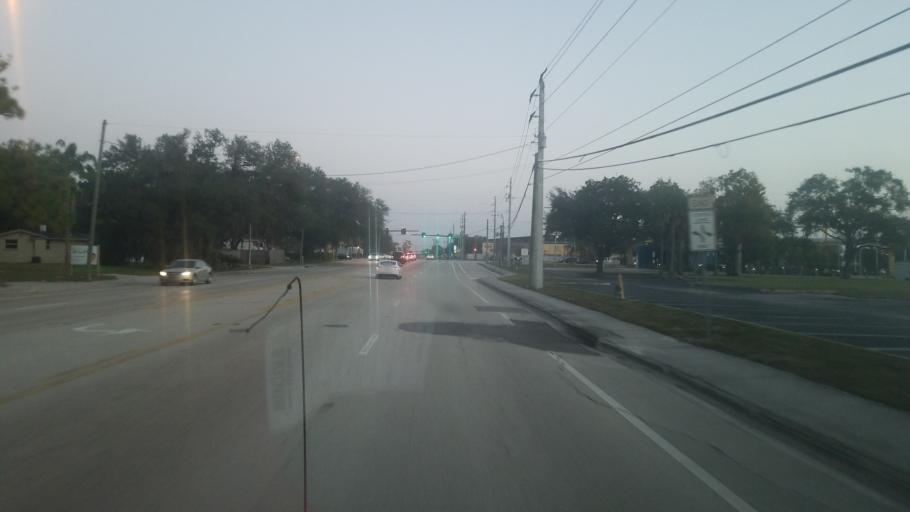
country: US
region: Florida
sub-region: Sarasota County
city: Fruitville
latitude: 27.3214
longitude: -82.4514
